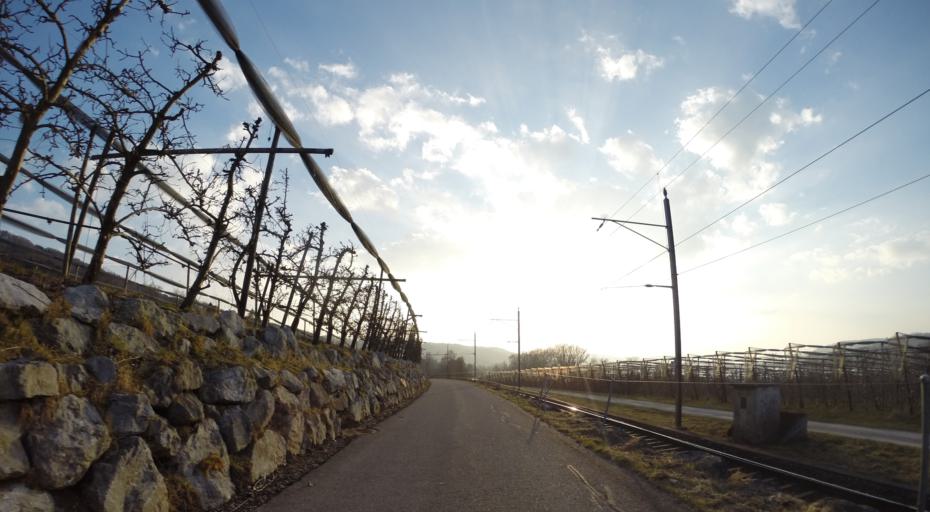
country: DE
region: Baden-Wuerttemberg
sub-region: Freiburg Region
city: Ohningen
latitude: 47.6504
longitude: 8.9320
